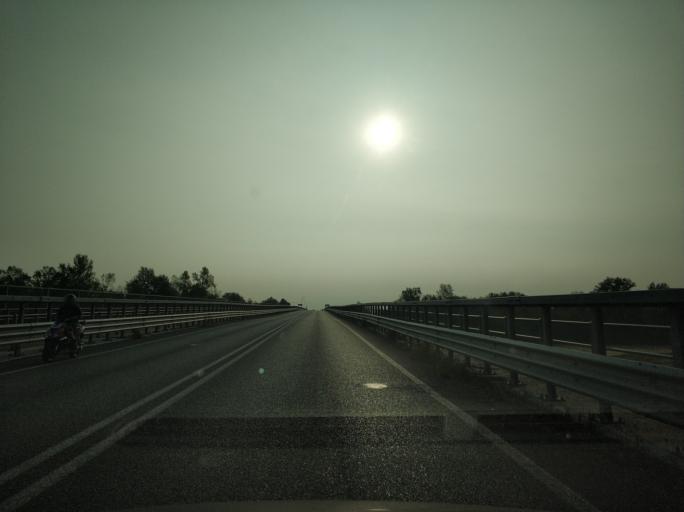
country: IT
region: Piedmont
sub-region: Provincia di Torino
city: Borgaro Torinese
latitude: 45.1492
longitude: 7.6377
